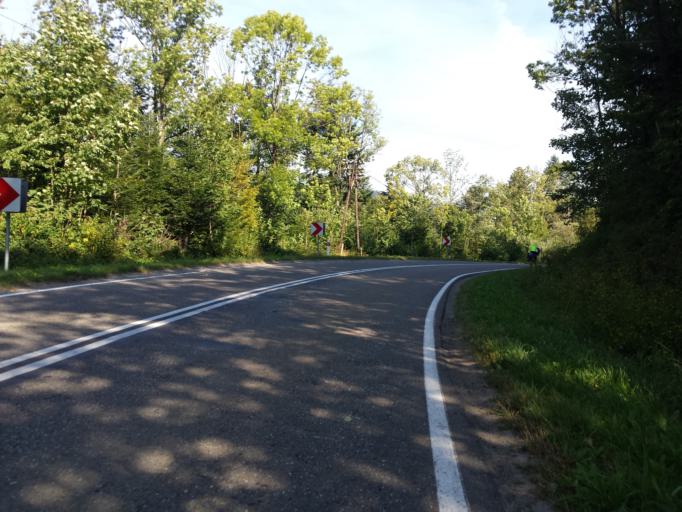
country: PL
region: Subcarpathian Voivodeship
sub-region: Powiat leski
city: Baligrod
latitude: 49.3069
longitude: 22.2764
